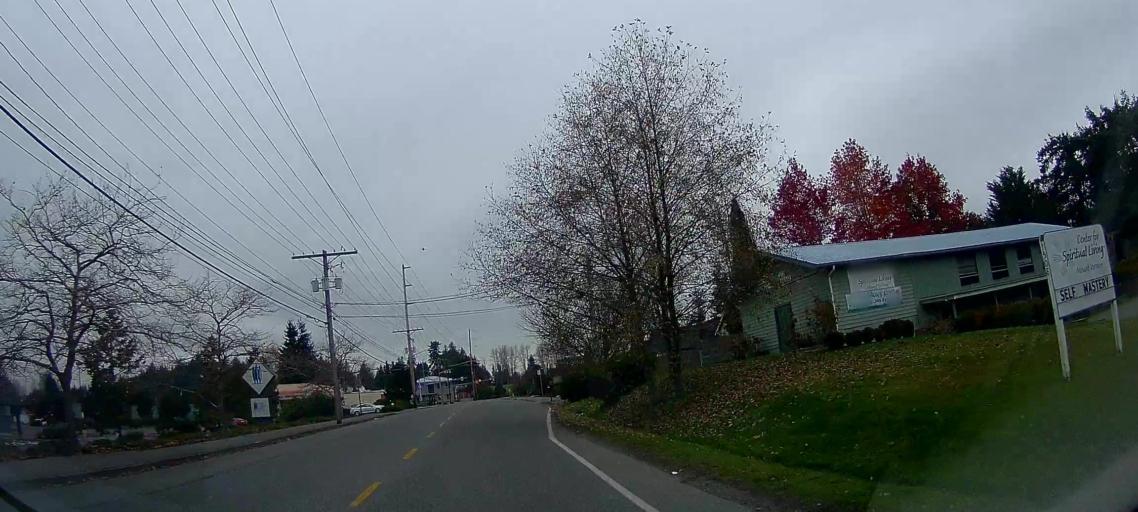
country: US
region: Washington
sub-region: Skagit County
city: Mount Vernon
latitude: 48.4336
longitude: -122.3187
